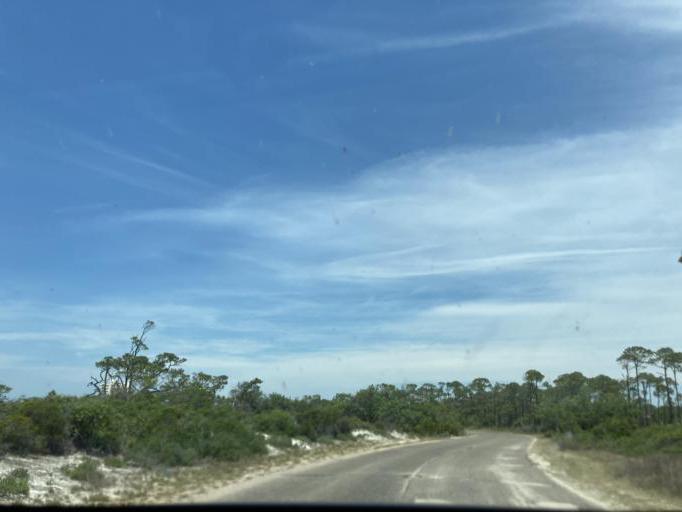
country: US
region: Florida
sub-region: Bay County
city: Lower Grand Lagoon
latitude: 30.1308
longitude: -85.7391
